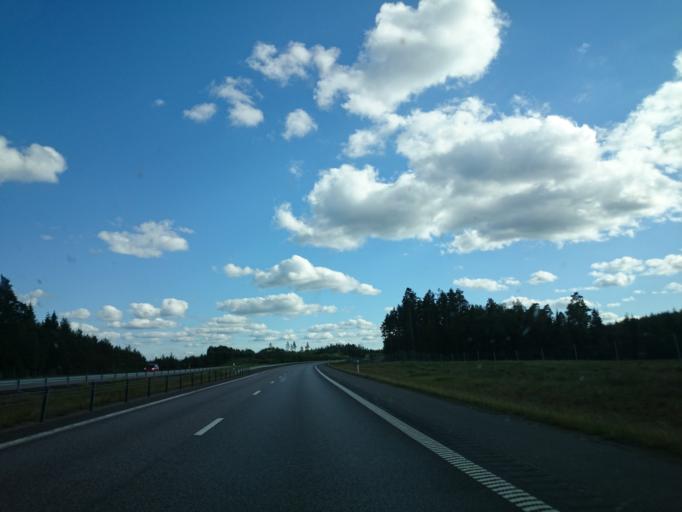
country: SE
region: Kronoberg
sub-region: Ljungby Kommun
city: Ljungby
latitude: 56.7641
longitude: 13.8808
